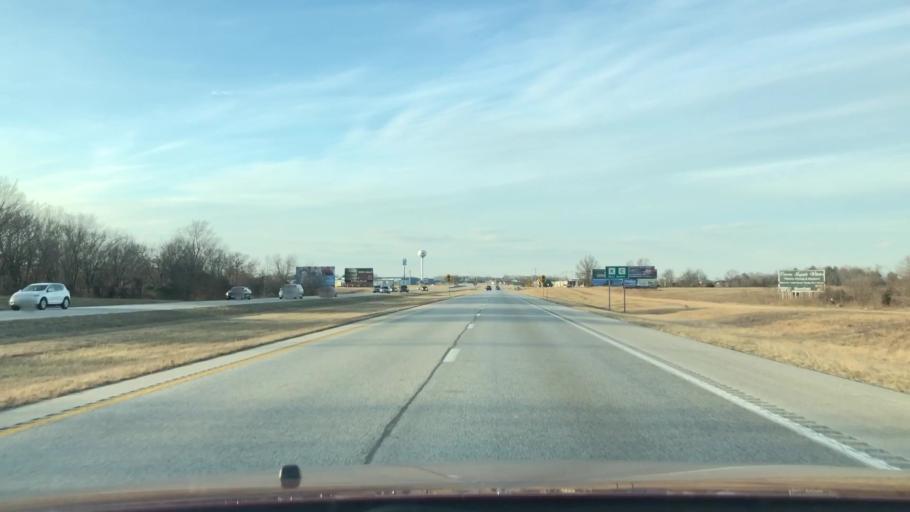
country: US
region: Missouri
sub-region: Webster County
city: Seymour
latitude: 37.1463
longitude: -92.7494
